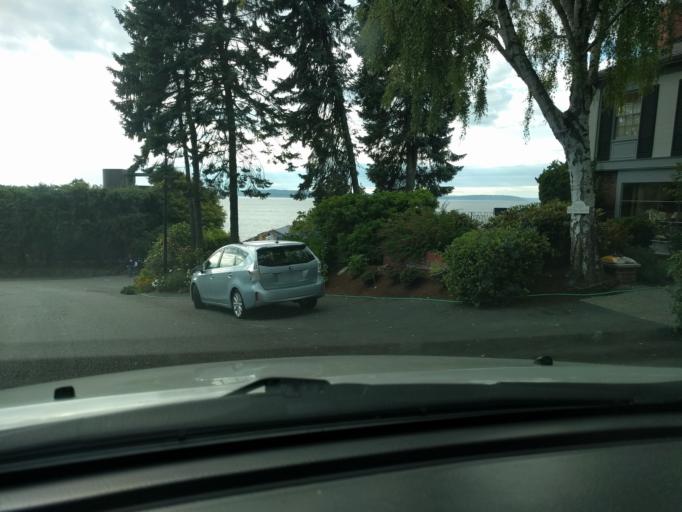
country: US
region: Washington
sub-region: King County
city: Shoreline
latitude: 47.7036
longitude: -122.3844
